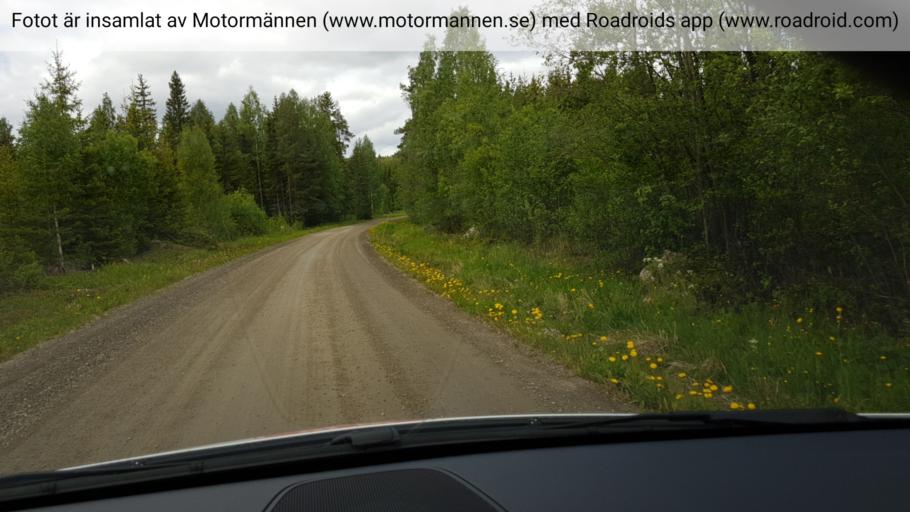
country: SE
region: Jaemtland
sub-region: Braecke Kommun
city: Braecke
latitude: 62.8027
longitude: 15.2309
